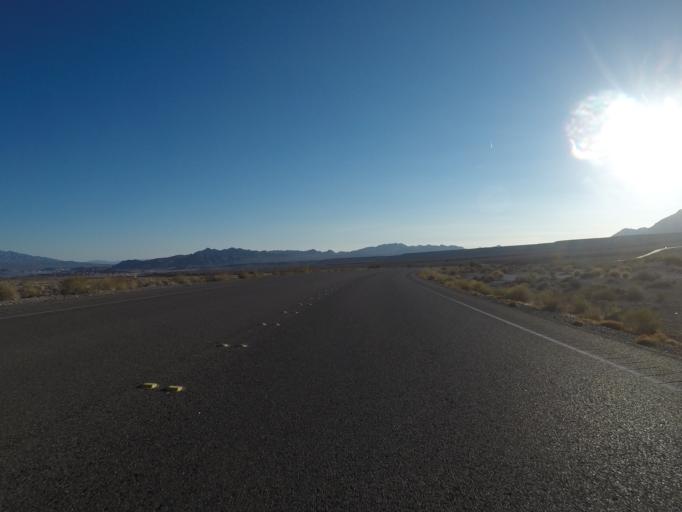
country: US
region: Nevada
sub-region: Clark County
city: Moapa Valley
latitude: 36.3718
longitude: -114.4435
